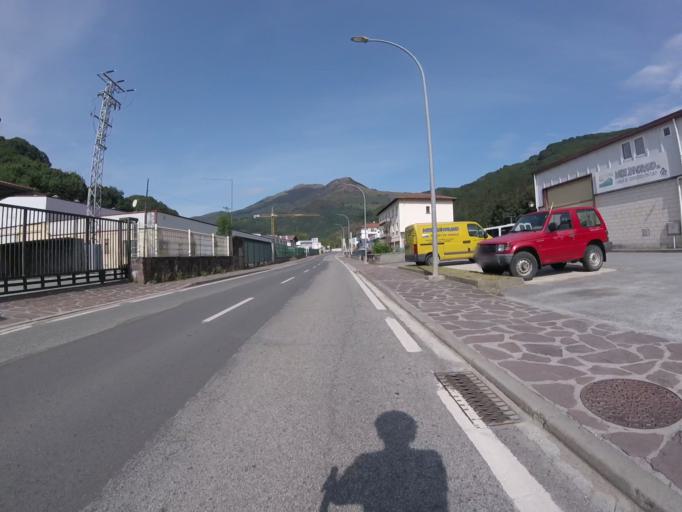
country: ES
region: Navarre
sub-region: Provincia de Navarra
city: Elgorriaga
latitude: 43.1344
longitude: -1.6773
